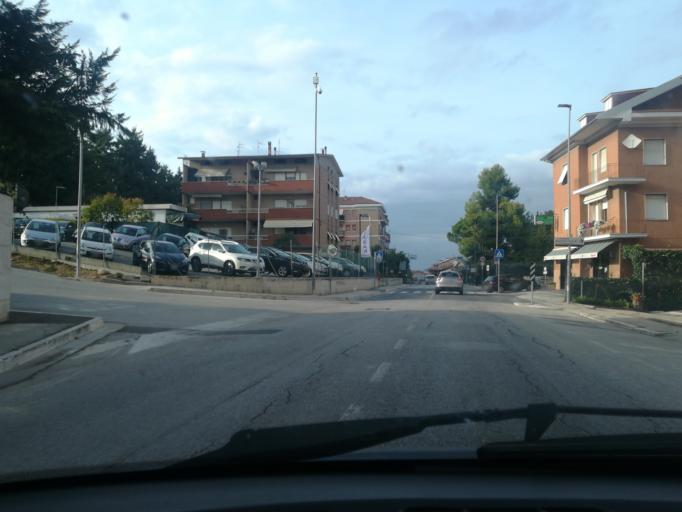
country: IT
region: The Marches
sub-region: Provincia di Macerata
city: Macerata
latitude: 43.3072
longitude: 13.4380
